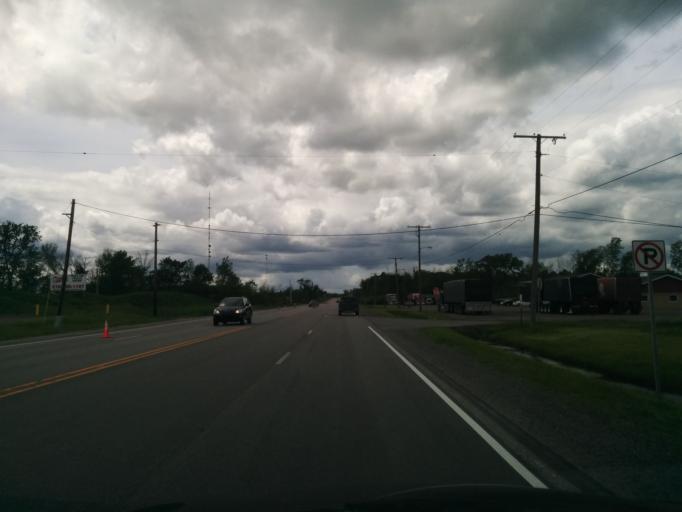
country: US
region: Indiana
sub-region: Porter County
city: Chesterton
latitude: 41.6369
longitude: -87.0377
